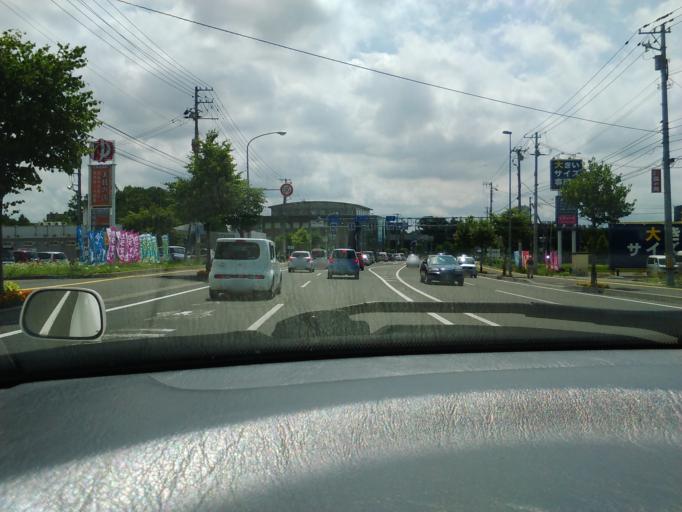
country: JP
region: Hokkaido
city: Ebetsu
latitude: 43.0530
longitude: 141.4854
